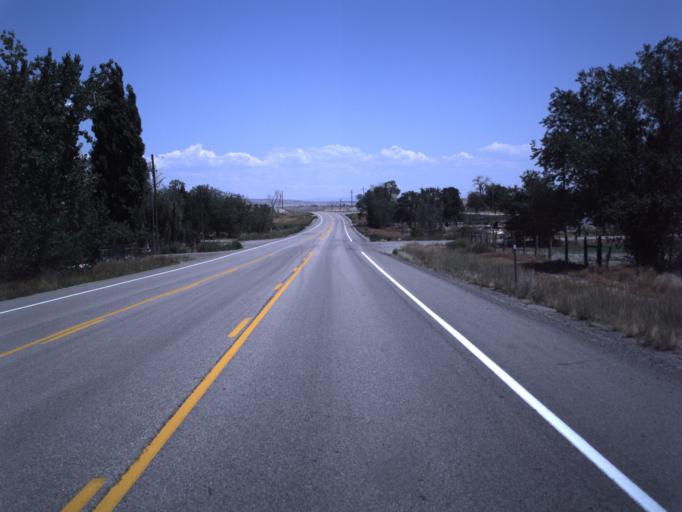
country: US
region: Utah
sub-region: Emery County
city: Ferron
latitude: 39.1343
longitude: -111.0992
